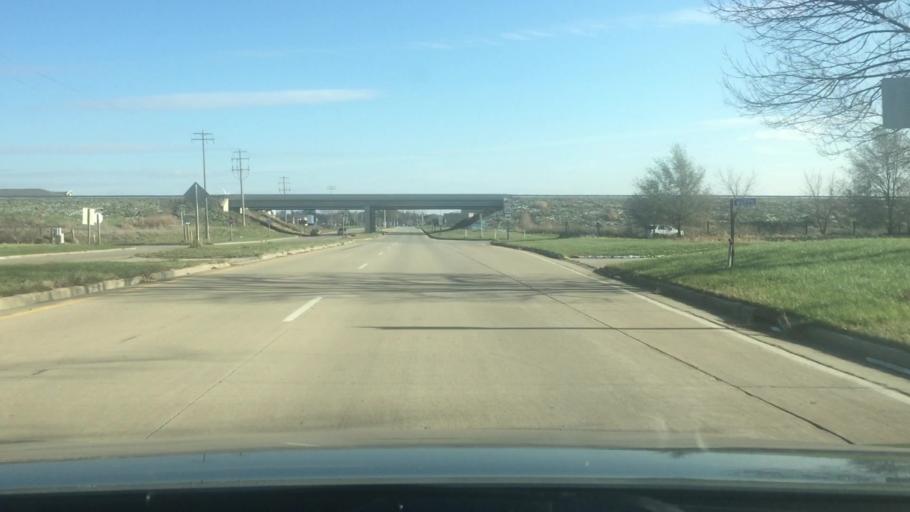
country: US
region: Wisconsin
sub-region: Jefferson County
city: Fort Atkinson
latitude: 42.9446
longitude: -88.8679
